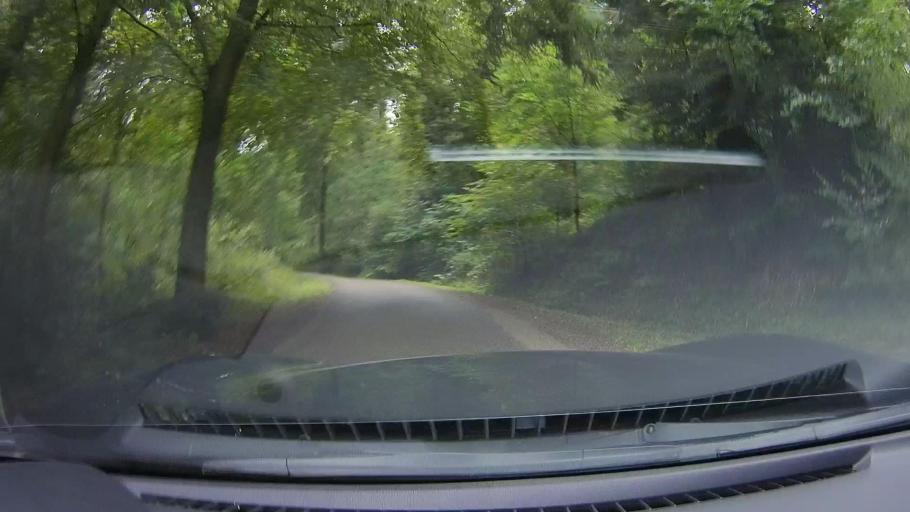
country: DE
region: Baden-Wuerttemberg
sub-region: Regierungsbezirk Stuttgart
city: Murrhardt
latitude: 48.9739
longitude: 9.5599
